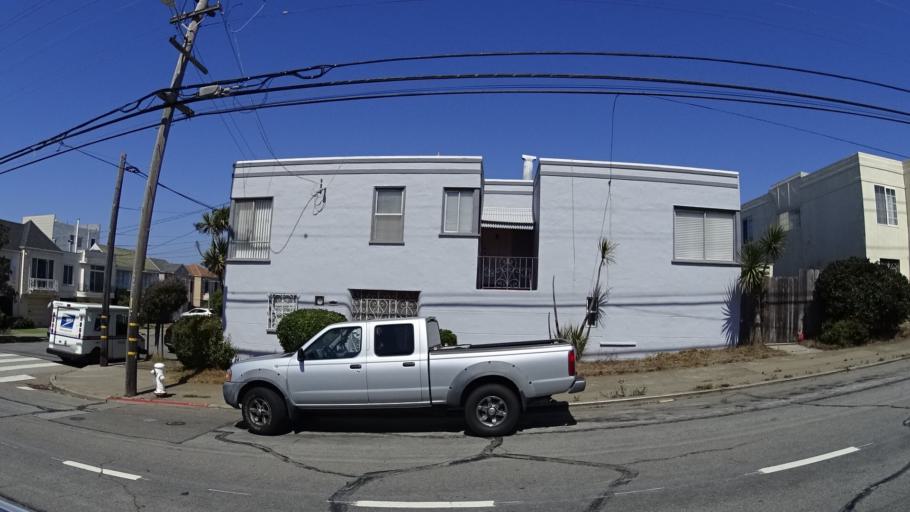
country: US
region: California
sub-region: San Mateo County
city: Daly City
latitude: 37.7521
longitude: -122.4837
